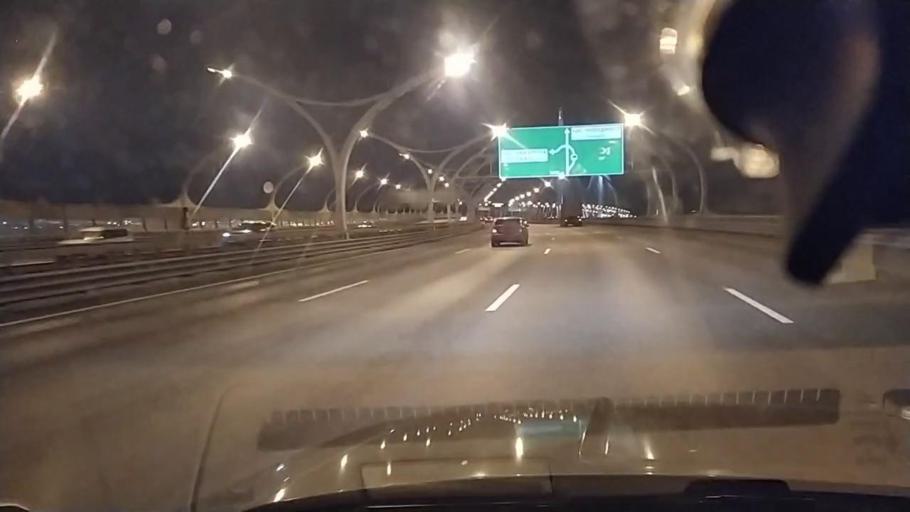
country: RU
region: St.-Petersburg
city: Staraya Derevnya
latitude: 59.9730
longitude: 30.2132
